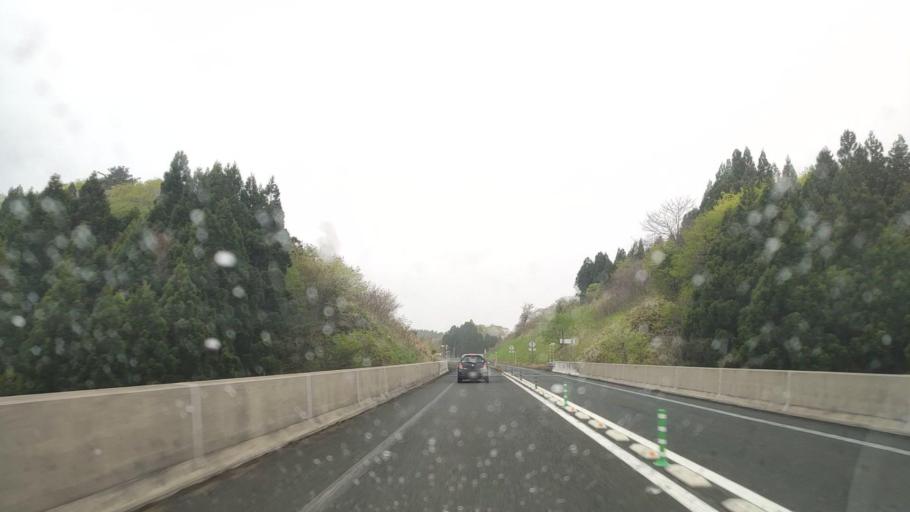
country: JP
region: Akita
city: Noshiromachi
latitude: 40.2073
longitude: 140.1703
